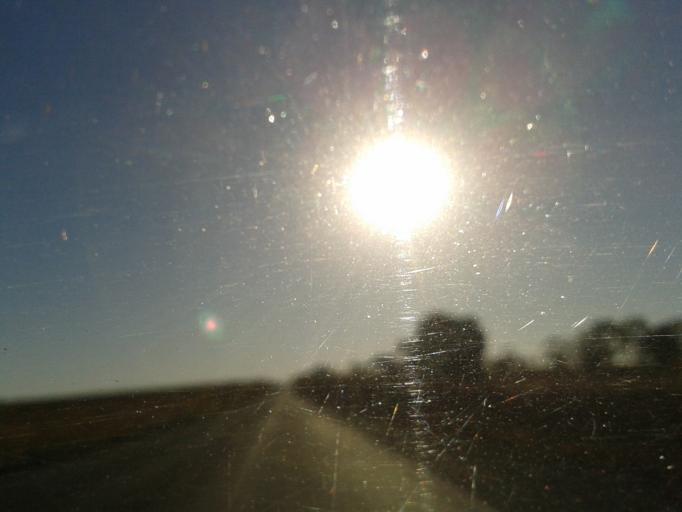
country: BR
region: Minas Gerais
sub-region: Santa Vitoria
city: Santa Vitoria
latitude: -19.1438
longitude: -50.1859
